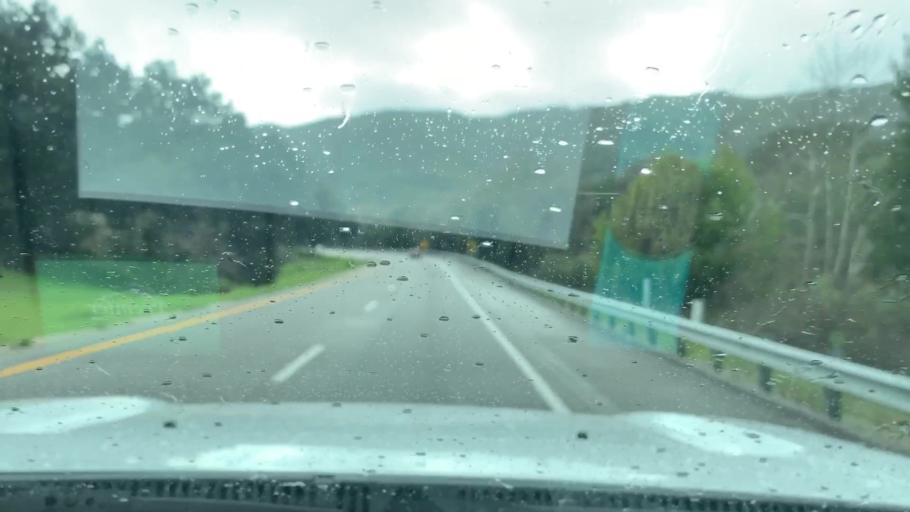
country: US
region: California
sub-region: San Luis Obispo County
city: Santa Margarita
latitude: 35.3729
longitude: -120.6403
